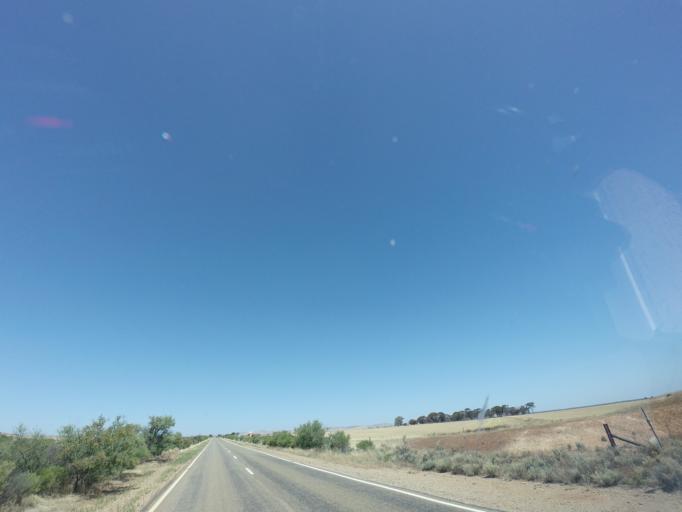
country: AU
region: South Australia
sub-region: Flinders Ranges
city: Quorn
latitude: -32.6987
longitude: 138.3829
